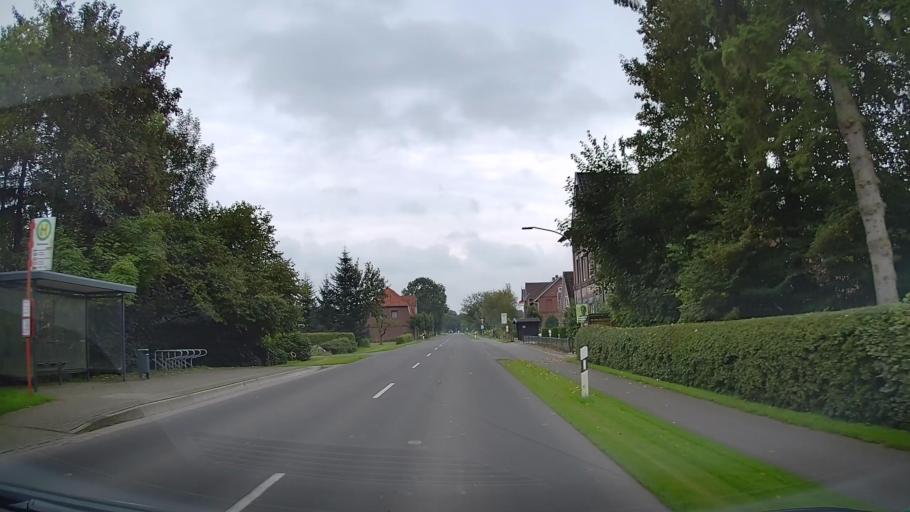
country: DE
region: Lower Saxony
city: Drochtersen
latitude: 53.7211
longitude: 9.3626
